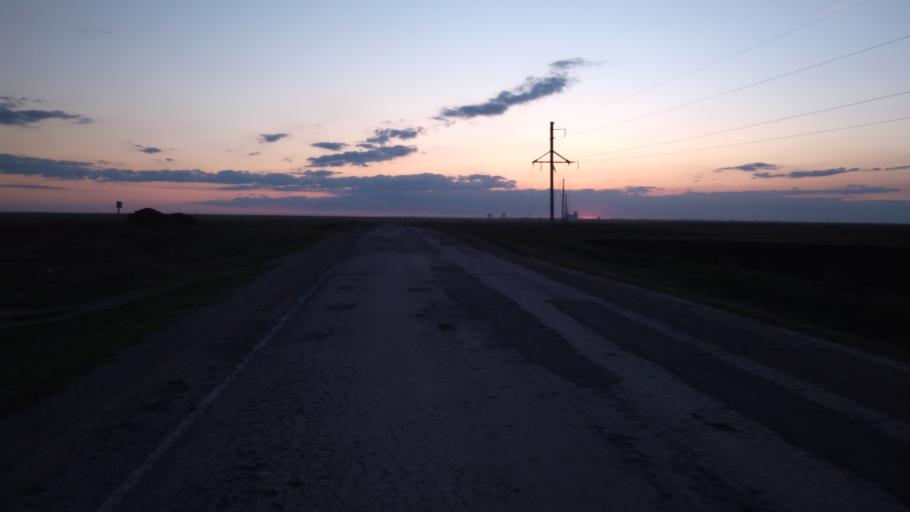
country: RU
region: Chelyabinsk
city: Troitsk
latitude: 54.0865
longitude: 61.6633
